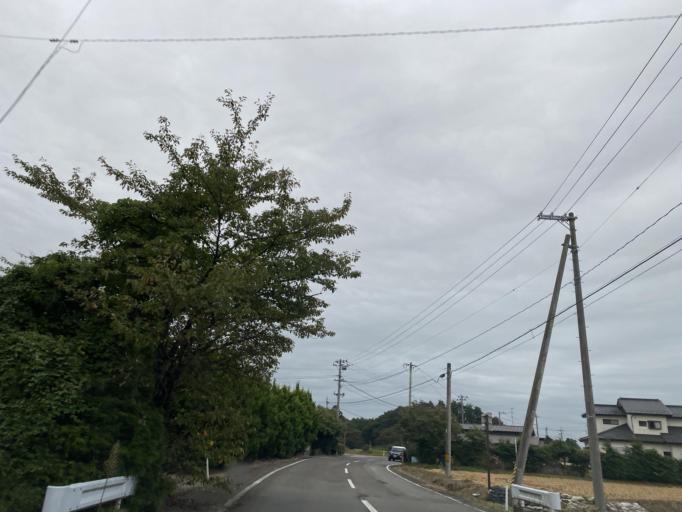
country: JP
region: Fukushima
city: Koriyama
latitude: 37.3615
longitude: 140.2594
